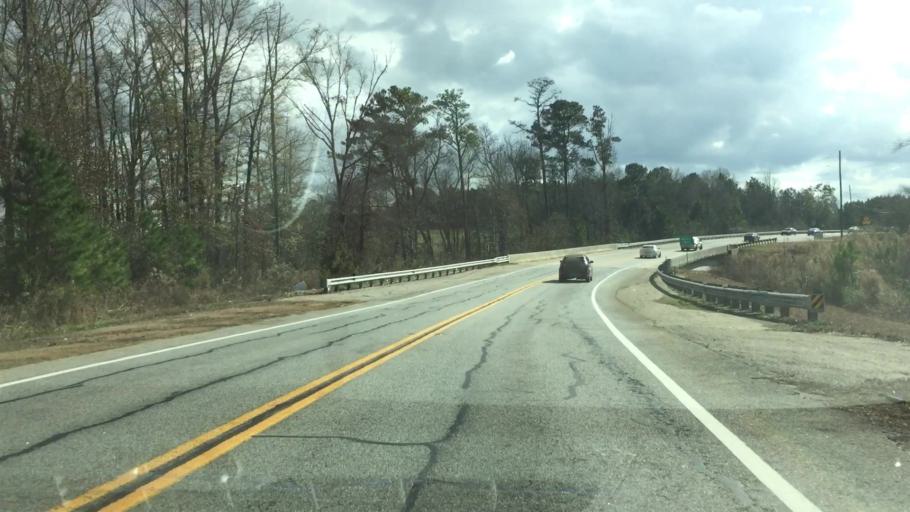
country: US
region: Georgia
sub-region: Henry County
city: McDonough
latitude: 33.4768
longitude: -84.1393
